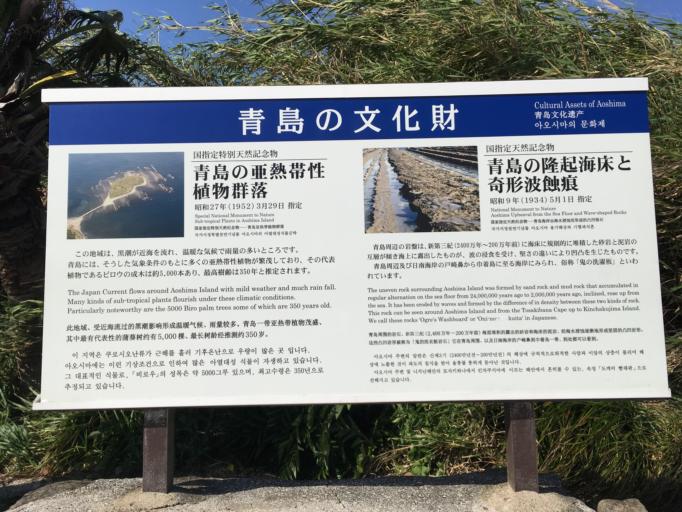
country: JP
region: Miyazaki
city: Miyazaki-shi
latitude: 31.8038
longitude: 131.4738
